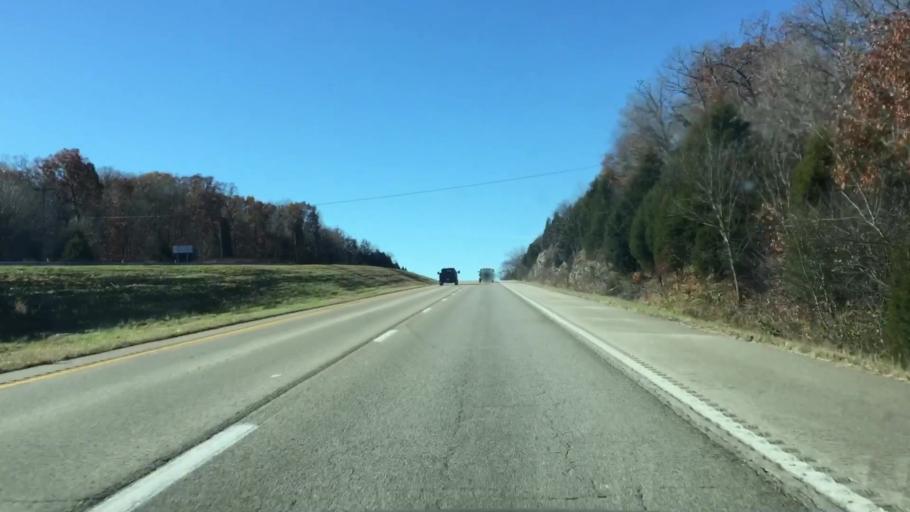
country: US
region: Missouri
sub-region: Cole County
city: Wardsville
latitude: 38.5162
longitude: -92.2376
